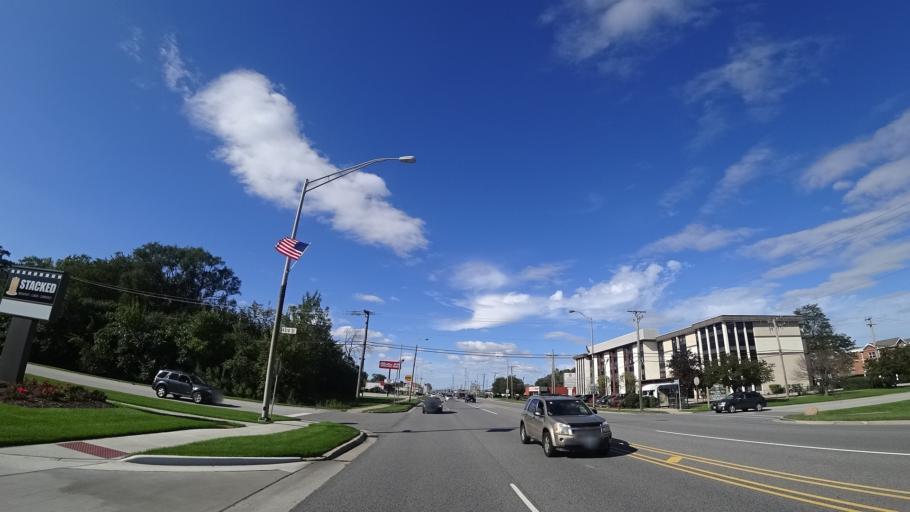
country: US
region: Illinois
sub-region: Cook County
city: Midlothian
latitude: 41.6324
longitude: -87.7376
